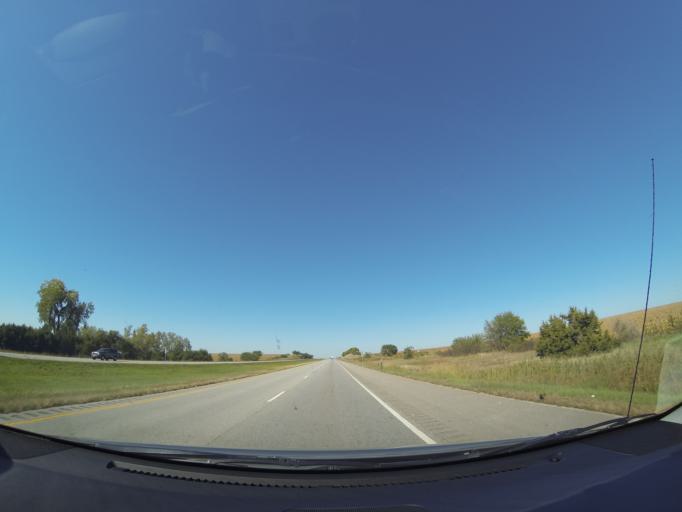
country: US
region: Nebraska
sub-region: Seward County
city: Seward
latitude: 40.8224
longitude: -97.1375
